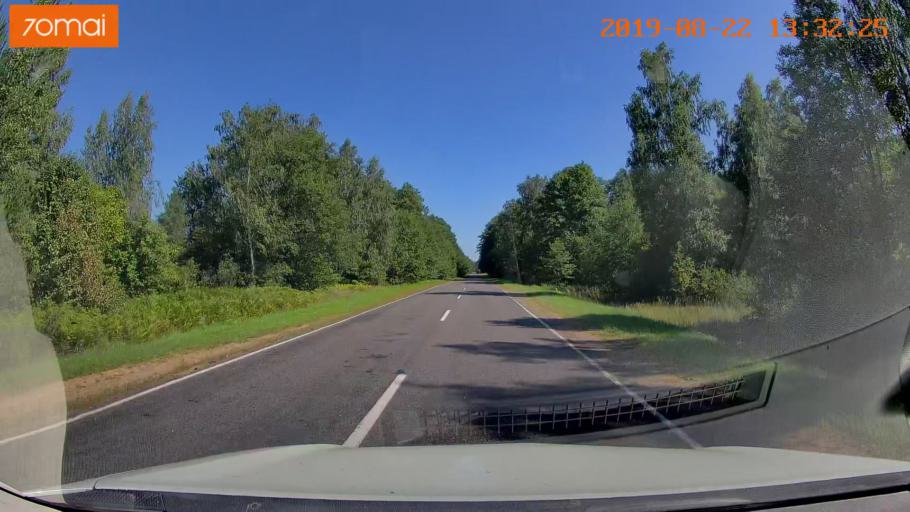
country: BY
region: Minsk
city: Staryya Darohi
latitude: 53.2171
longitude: 28.2033
